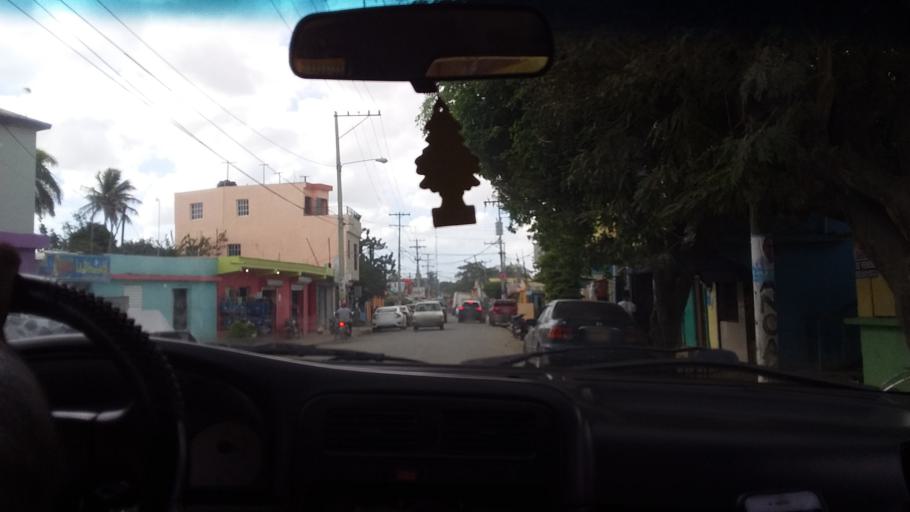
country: DO
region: Santo Domingo
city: Guerra
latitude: 18.5590
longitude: -69.7011
